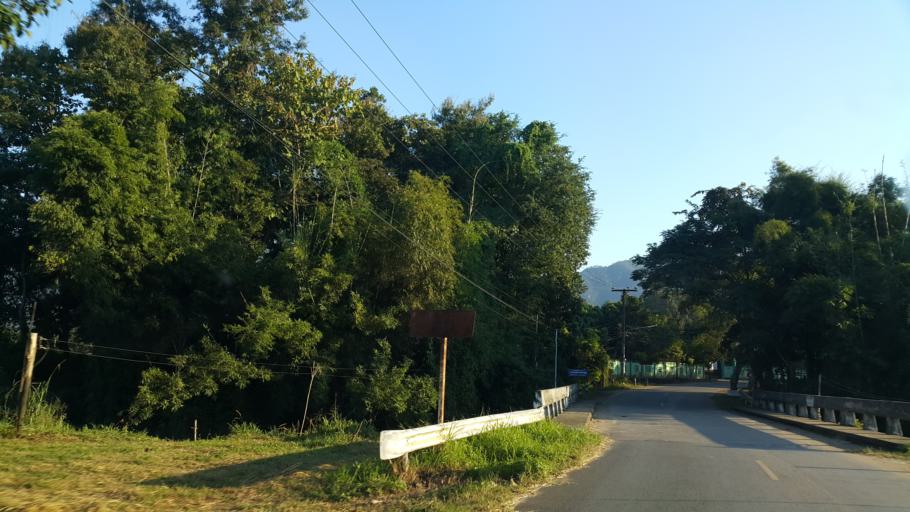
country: TH
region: Chiang Mai
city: Mae On
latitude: 18.7531
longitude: 99.2433
